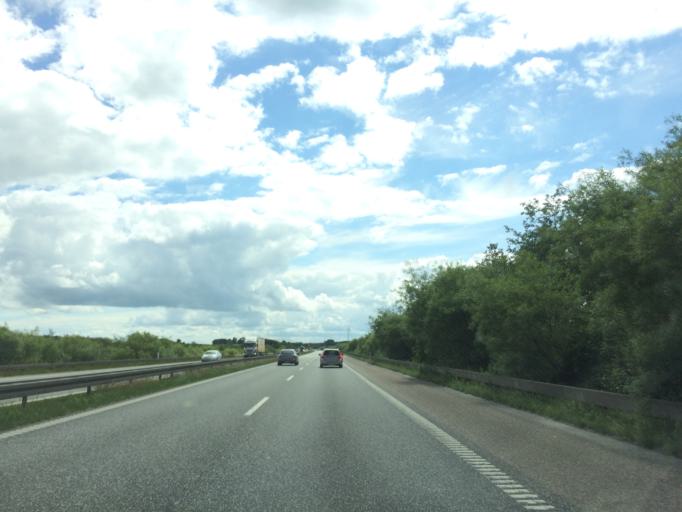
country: DK
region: North Denmark
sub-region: Mariagerfjord Kommune
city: Hobro
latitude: 56.7011
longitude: 9.7292
